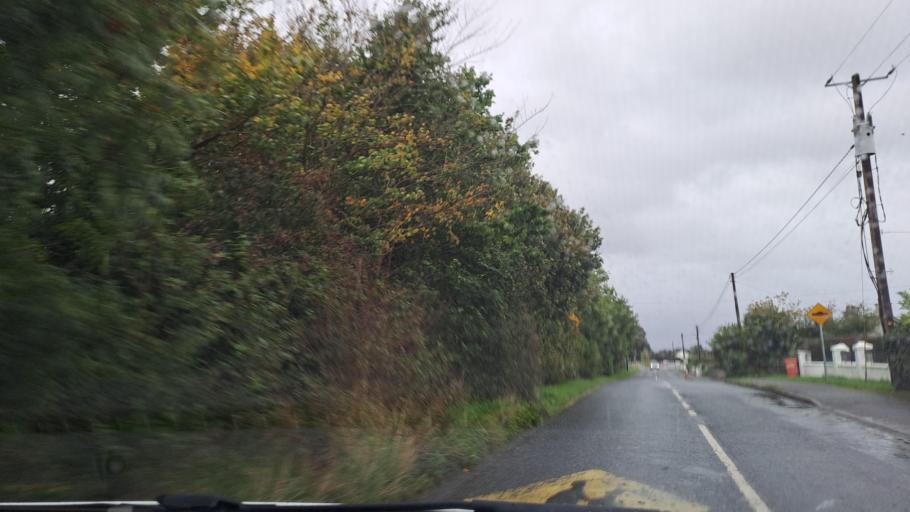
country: IE
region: Leinster
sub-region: Lu
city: Dundalk
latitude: 53.9645
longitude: -6.4083
